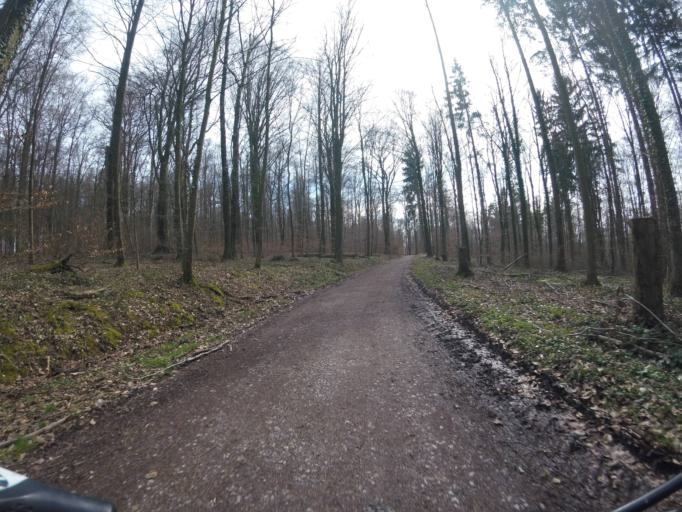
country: DE
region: Baden-Wuerttemberg
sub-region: Regierungsbezirk Stuttgart
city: Aspach
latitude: 48.9763
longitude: 9.4247
